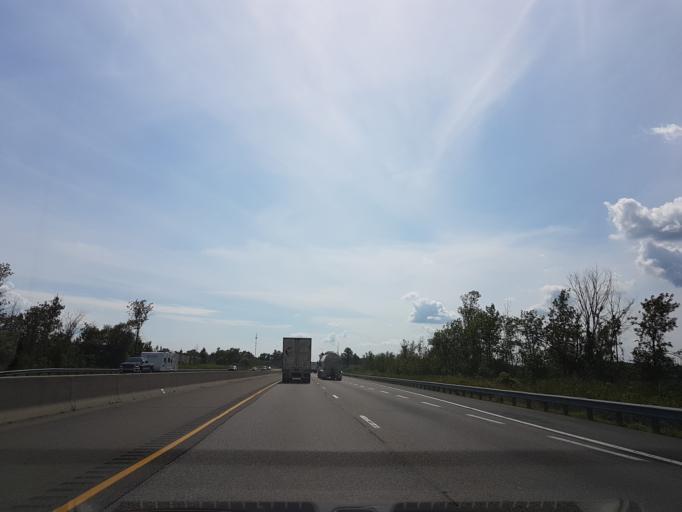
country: CA
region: Ontario
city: Prescott
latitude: 44.7269
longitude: -75.5194
